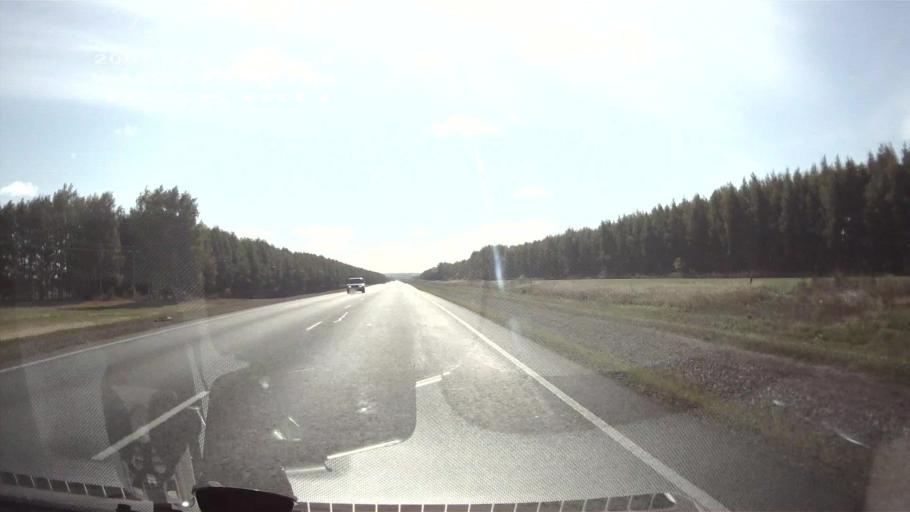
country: RU
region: Ulyanovsk
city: Tsil'na
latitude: 54.5517
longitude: 47.9407
